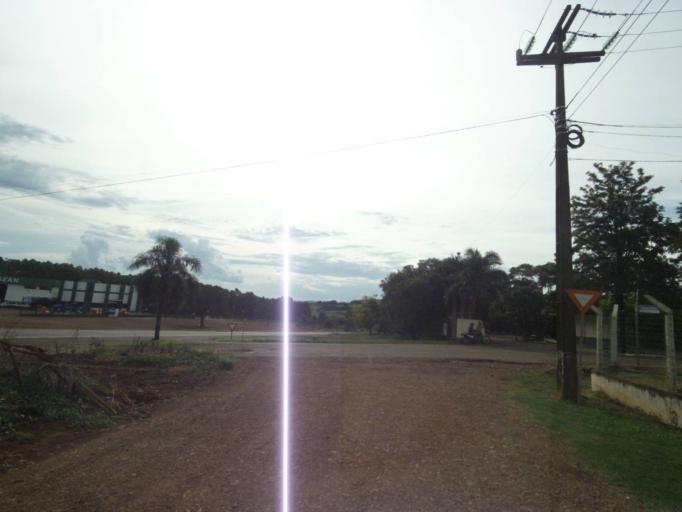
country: BR
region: Parana
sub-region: Guaraniacu
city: Guaraniacu
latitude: -25.1034
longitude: -52.8786
